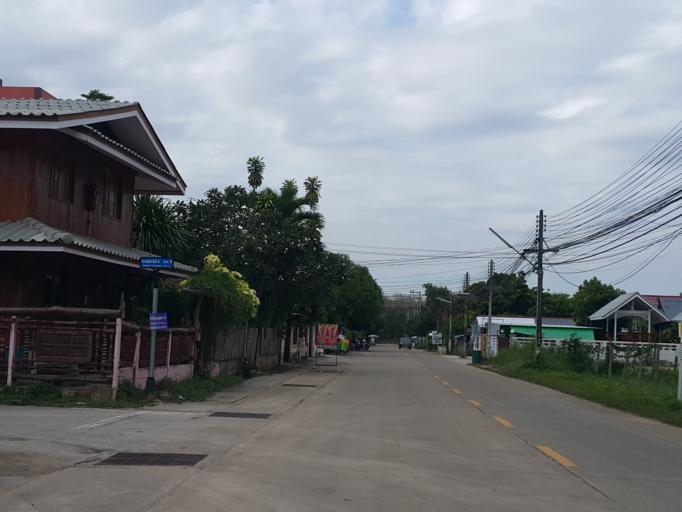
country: TH
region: Lampang
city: Lampang
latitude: 18.2762
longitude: 99.4959
